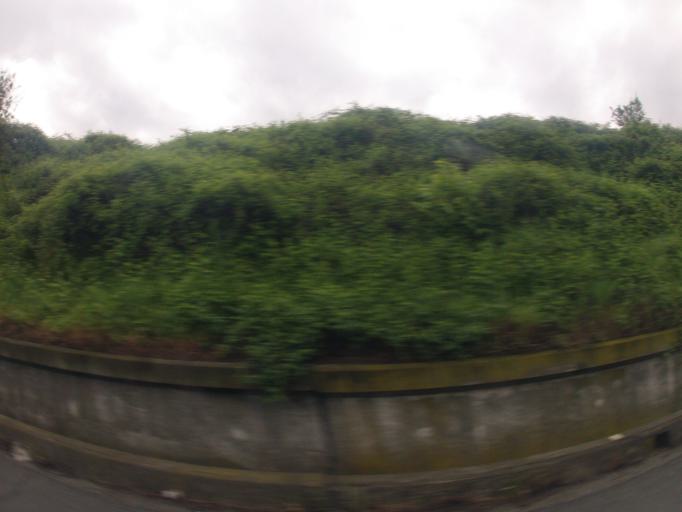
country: IT
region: Piedmont
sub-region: Provincia di Torino
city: La Loggia
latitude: 44.9469
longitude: 7.6791
